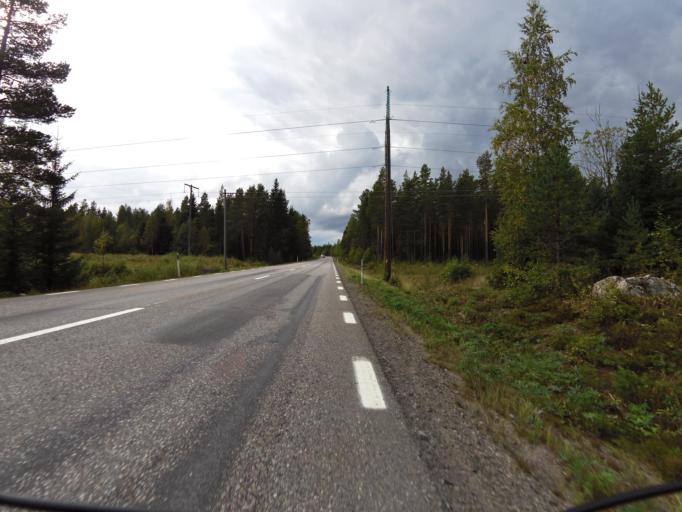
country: SE
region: Gaevleborg
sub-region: Gavle Kommun
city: Norrsundet
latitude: 60.9024
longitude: 16.9839
